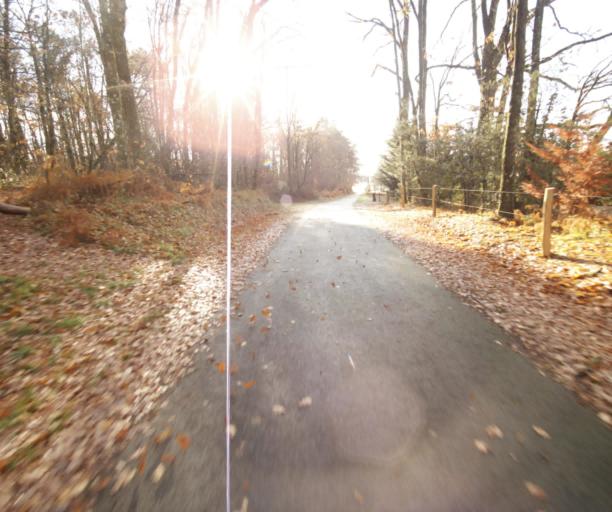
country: FR
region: Limousin
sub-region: Departement de la Correze
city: Saint-Mexant
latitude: 45.2479
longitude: 1.6274
